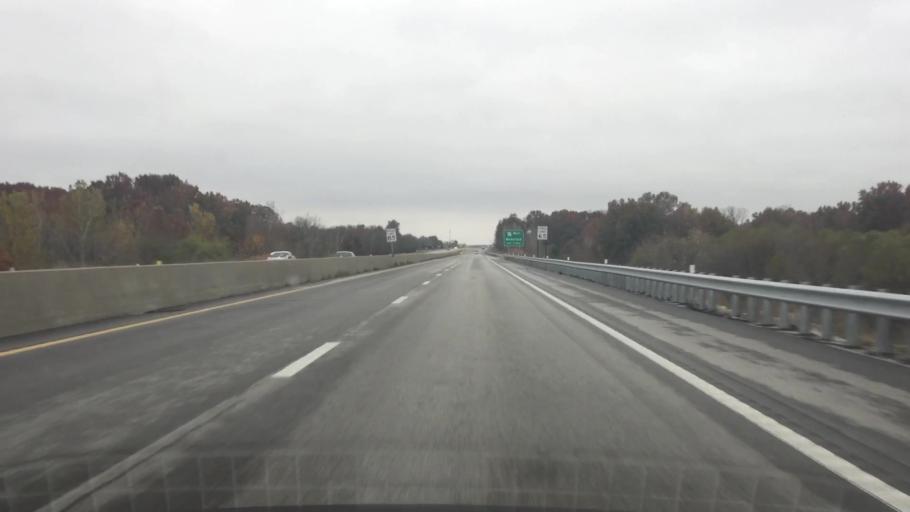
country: US
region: Missouri
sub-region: Henry County
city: Clinton
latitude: 38.2705
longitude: -93.7601
